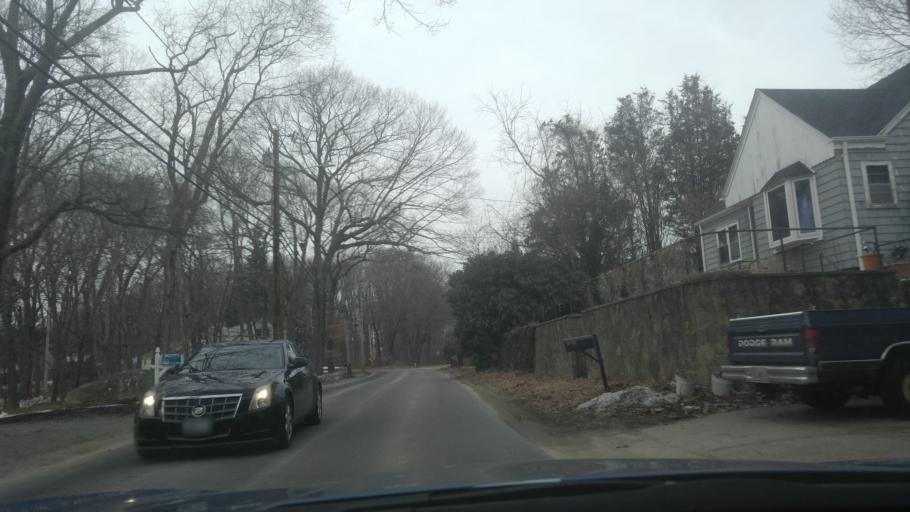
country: US
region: Rhode Island
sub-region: Kent County
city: West Warwick
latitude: 41.6765
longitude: -71.5194
